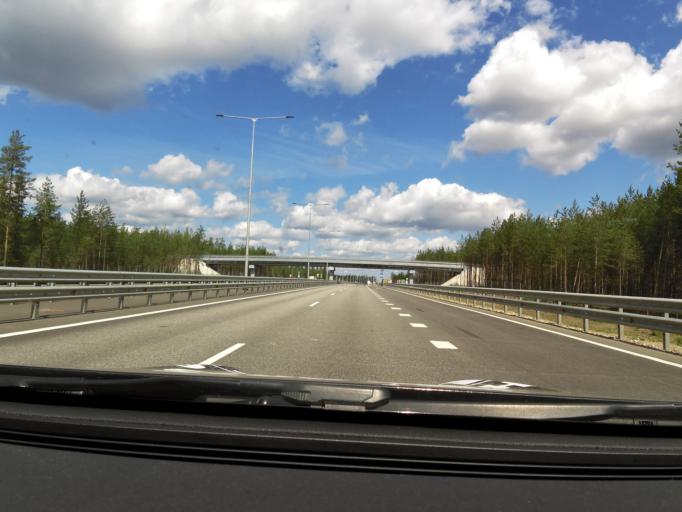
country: RU
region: Tverskaya
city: Krasnomayskiy
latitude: 57.5258
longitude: 34.2772
